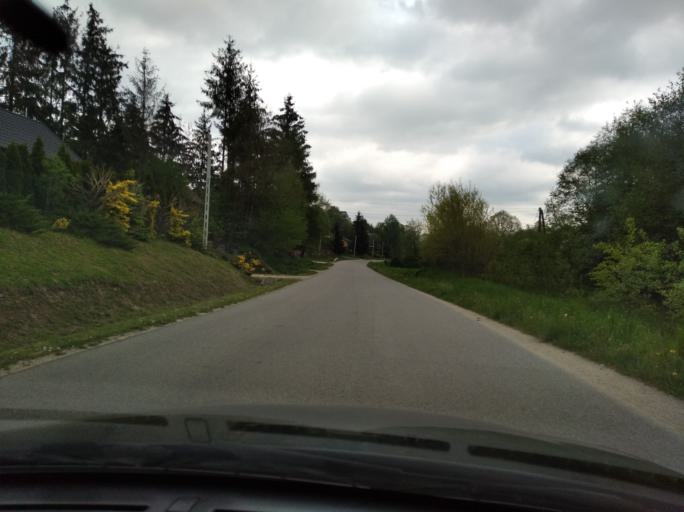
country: PL
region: Subcarpathian Voivodeship
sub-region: Powiat debicki
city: Leki Gorne
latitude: 49.9749
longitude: 21.1992
